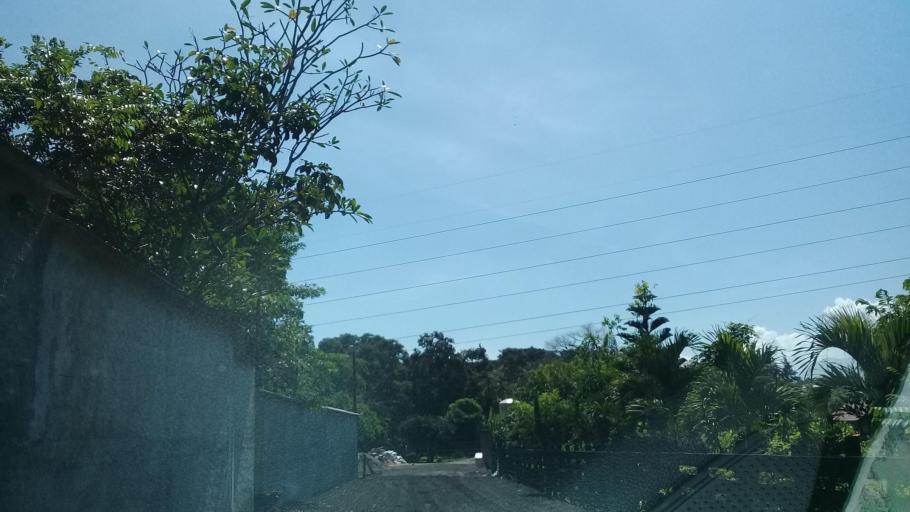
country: MX
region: Veracruz
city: Amatlan de los Reyes
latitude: 18.8541
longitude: -96.9220
